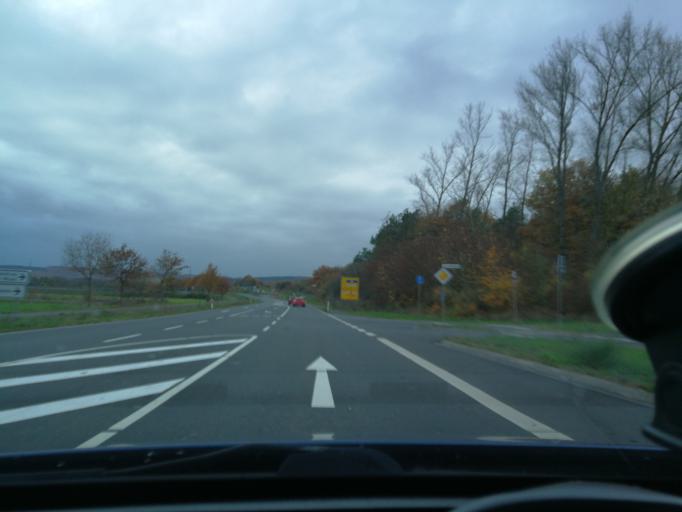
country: DE
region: Rheinland-Pfalz
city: Altrich
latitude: 49.9742
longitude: 6.9283
